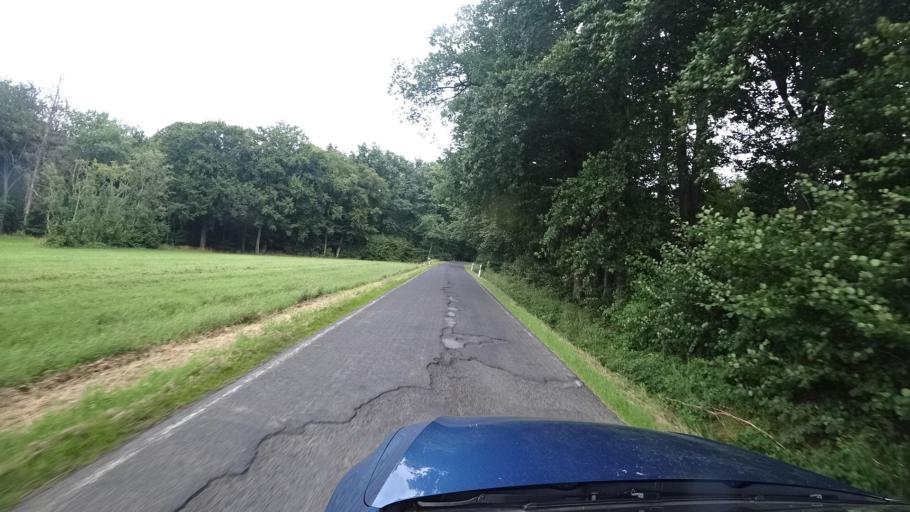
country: DE
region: Rheinland-Pfalz
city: Ziegenhain
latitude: 50.6823
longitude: 7.5255
